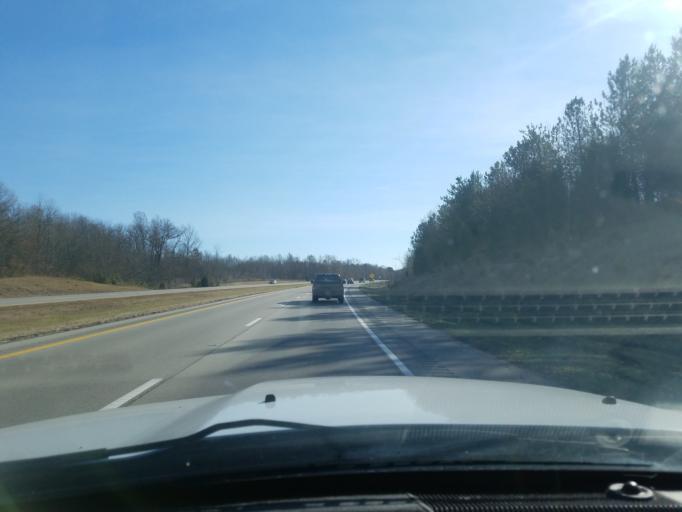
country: US
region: Ohio
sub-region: Brown County
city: Mount Orab
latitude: 39.0118
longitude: -83.7941
